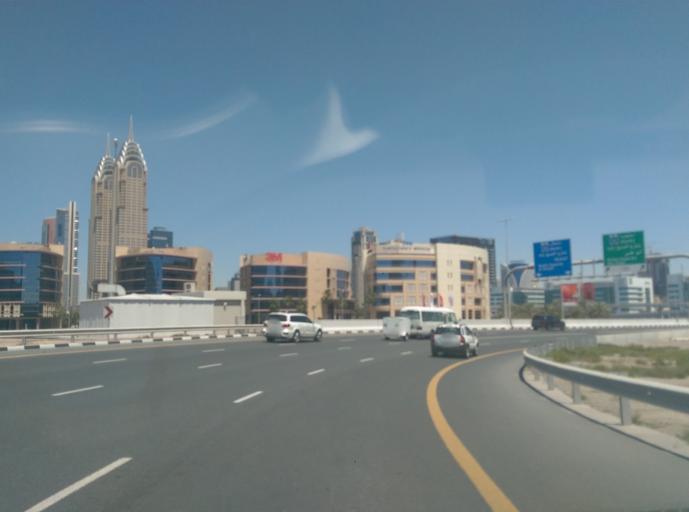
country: AE
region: Dubai
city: Dubai
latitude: 25.0969
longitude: 55.1616
